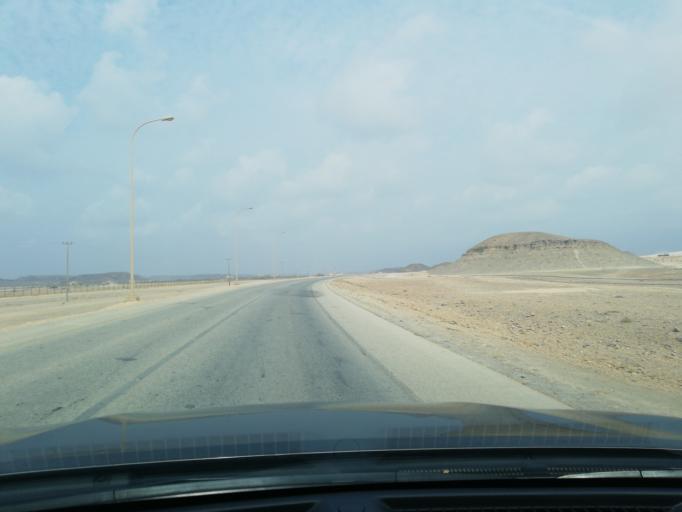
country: OM
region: Zufar
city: Salalah
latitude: 16.9460
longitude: 53.9496
